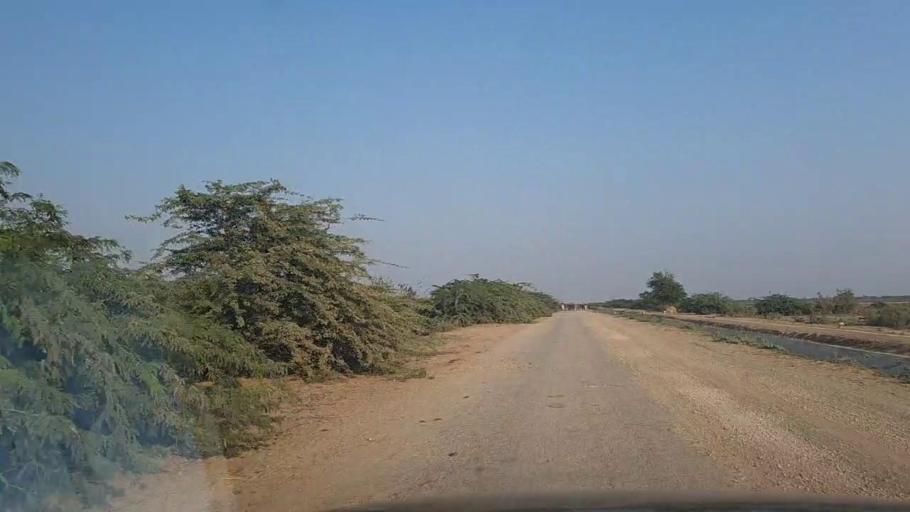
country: PK
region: Sindh
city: Keti Bandar
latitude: 24.2651
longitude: 67.5524
